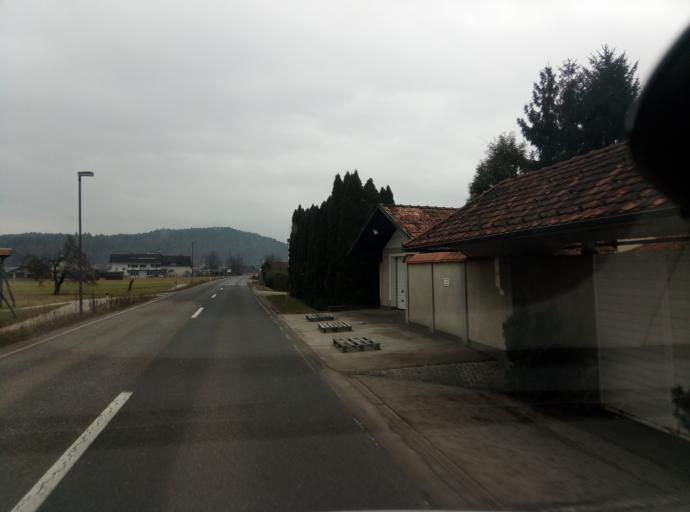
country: SI
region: Trzin
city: Trzin
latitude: 46.1029
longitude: 14.5483
